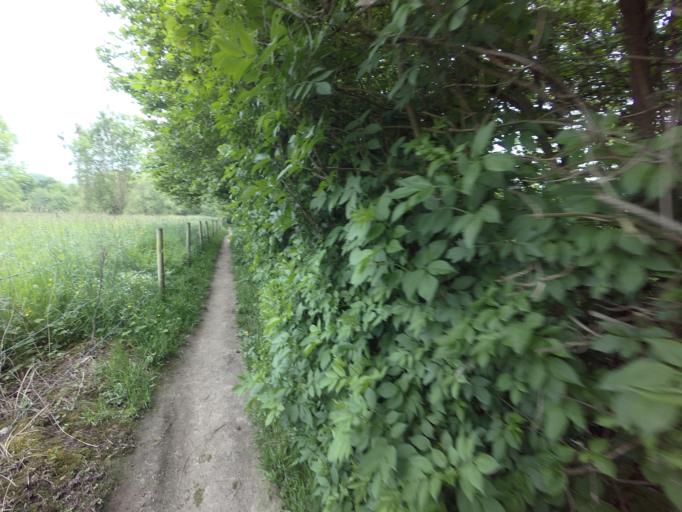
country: BE
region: Wallonia
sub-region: Province de Liege
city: Plombieres
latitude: 50.7573
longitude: 5.9233
